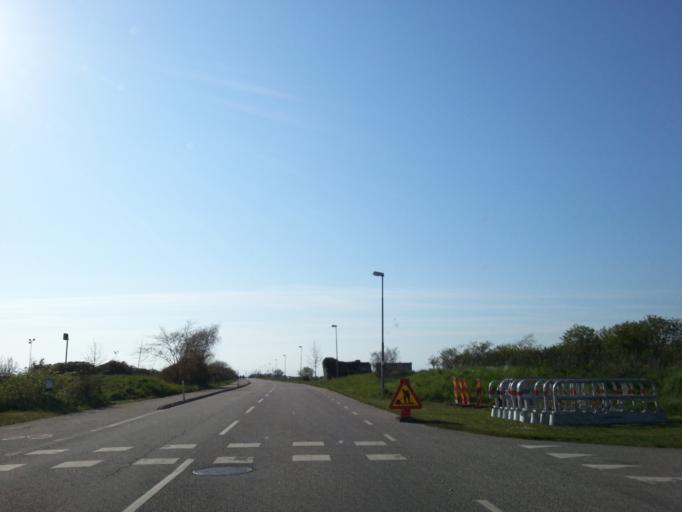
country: SE
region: Skane
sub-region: Vellinge Kommun
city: Skanor med Falsterbo
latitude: 55.4142
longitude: 12.8435
